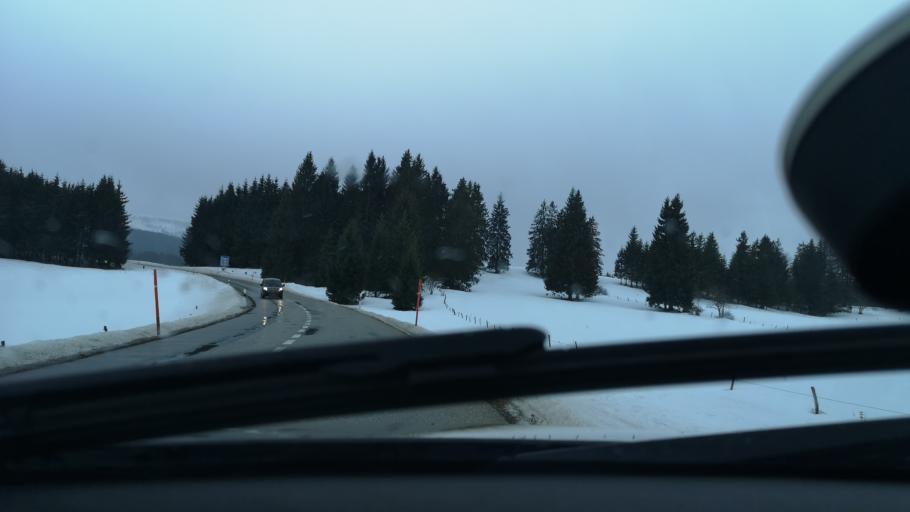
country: FR
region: Franche-Comte
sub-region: Departement du Doubs
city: Les Fourgs
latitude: 46.8212
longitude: 6.4402
